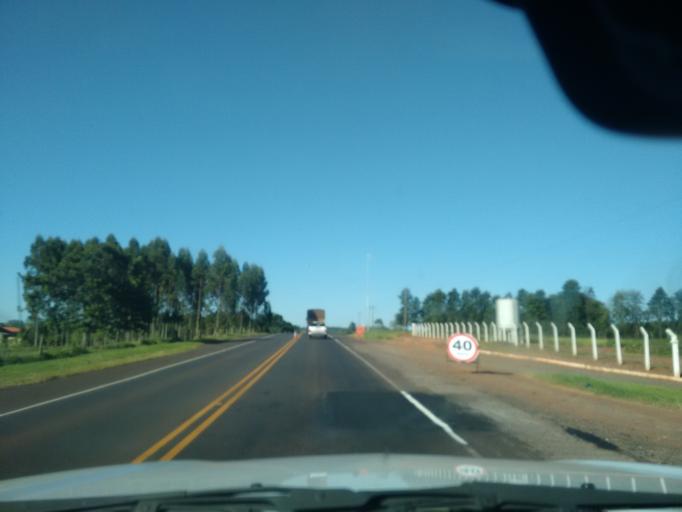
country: PY
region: Canindeyu
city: Salto del Guaira
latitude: -23.9620
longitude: -54.3216
